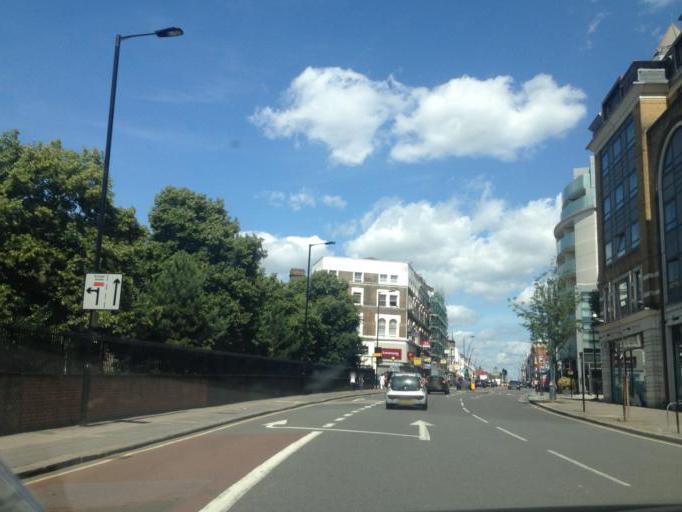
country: GB
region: England
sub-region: Greater London
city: Belsize Park
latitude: 51.5356
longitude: -0.1906
